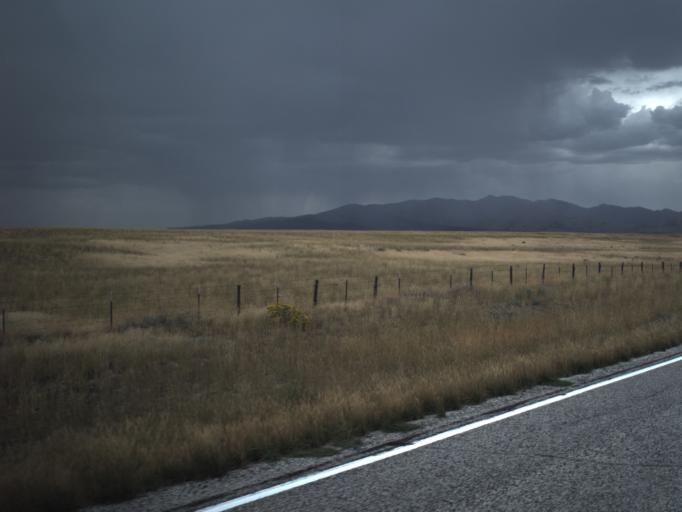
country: US
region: Idaho
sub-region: Oneida County
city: Malad City
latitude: 41.9212
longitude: -113.0950
